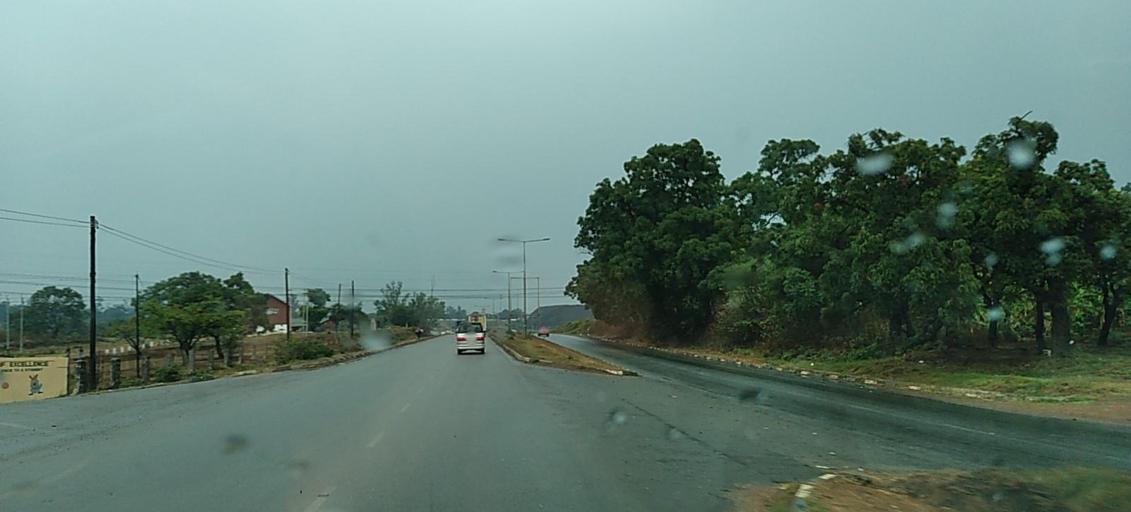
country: ZM
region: Copperbelt
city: Kitwe
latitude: -12.8304
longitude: 28.2148
